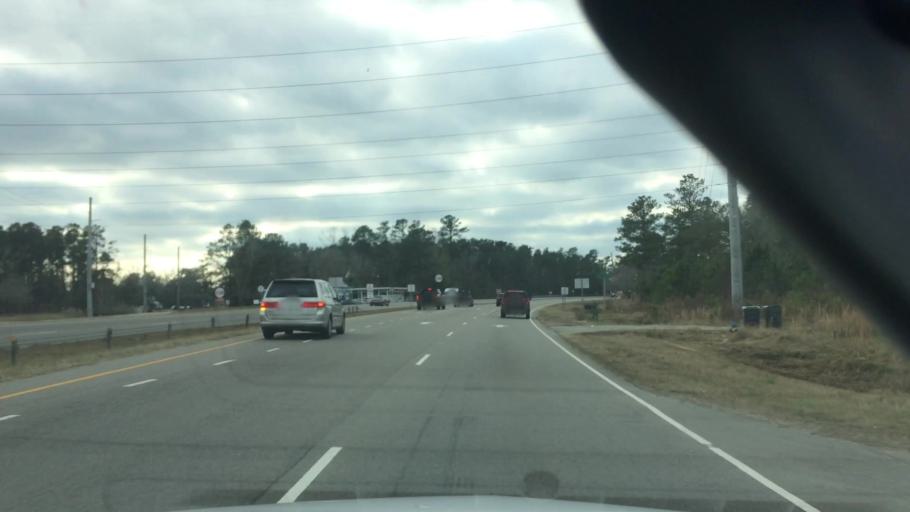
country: US
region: North Carolina
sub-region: Brunswick County
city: Bolivia
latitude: 34.0208
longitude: -78.2657
